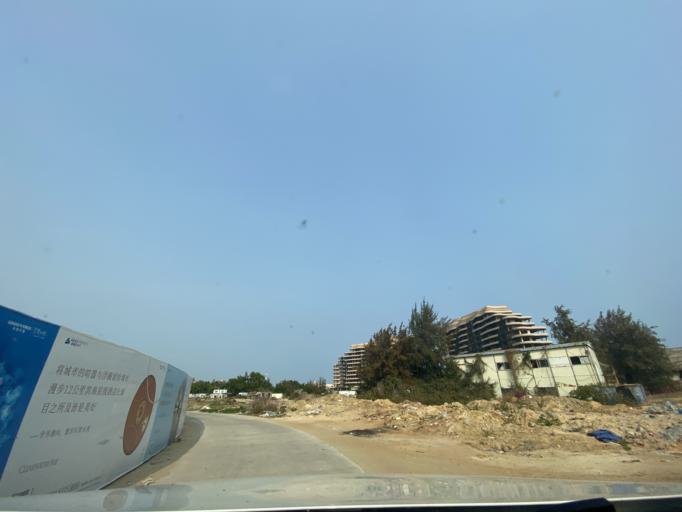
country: CN
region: Hainan
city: Yingzhou
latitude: 18.3931
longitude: 109.8550
